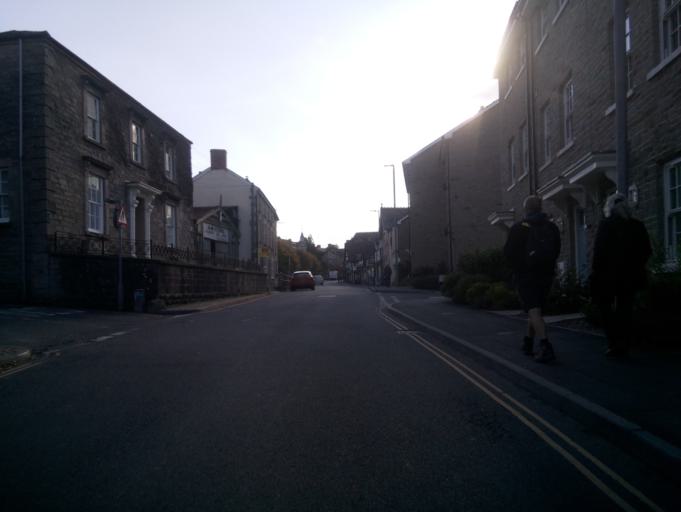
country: GB
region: Wales
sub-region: Sir Powys
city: Hay
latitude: 52.0765
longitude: -3.1254
